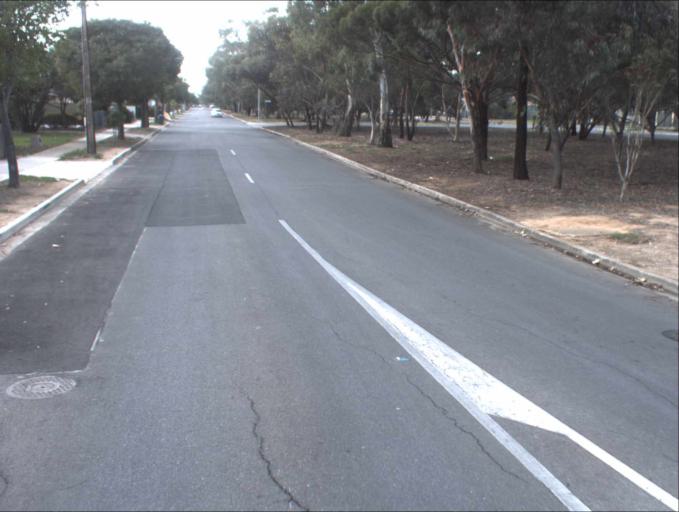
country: AU
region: South Australia
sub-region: Port Adelaide Enfield
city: Enfield
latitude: -34.8583
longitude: 138.6232
